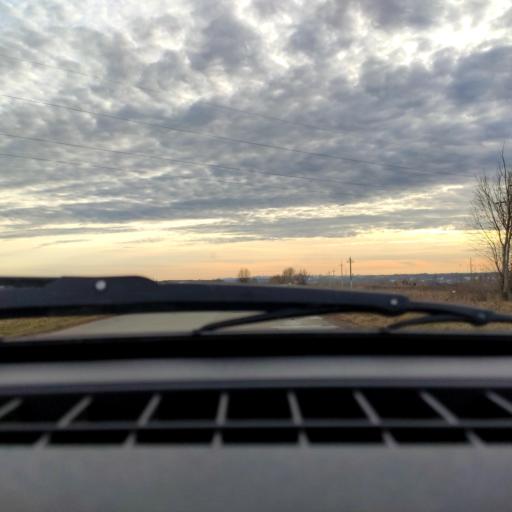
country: RU
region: Bashkortostan
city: Blagoveshchensk
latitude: 54.8952
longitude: 56.1516
